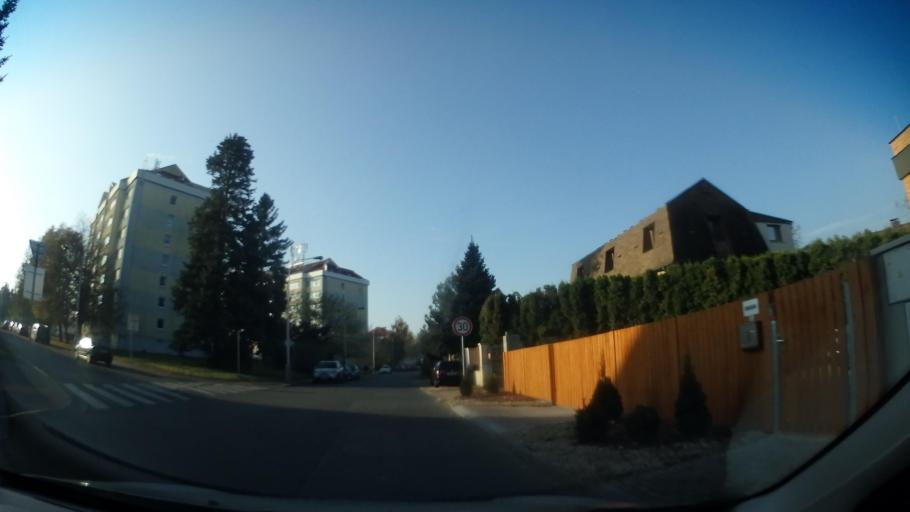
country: CZ
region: Central Bohemia
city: Sestajovice
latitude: 50.0722
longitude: 14.6794
